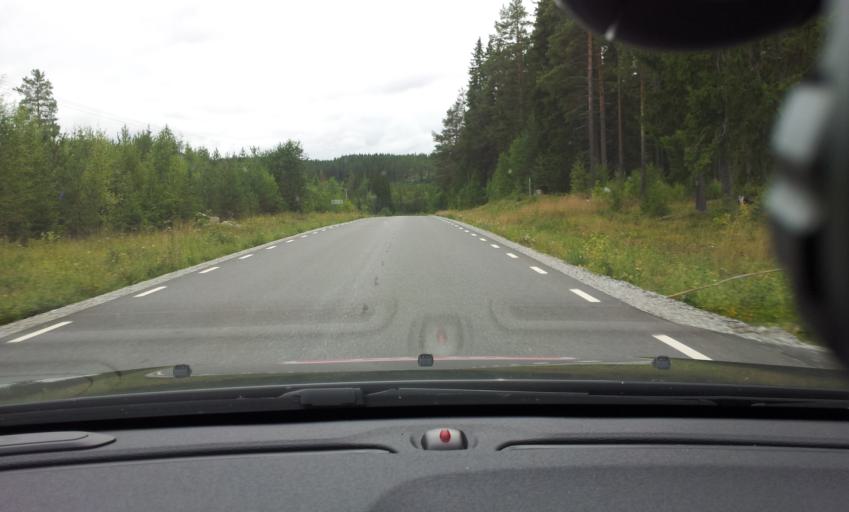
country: SE
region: Jaemtland
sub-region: Braecke Kommun
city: Braecke
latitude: 63.1423
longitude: 15.5354
